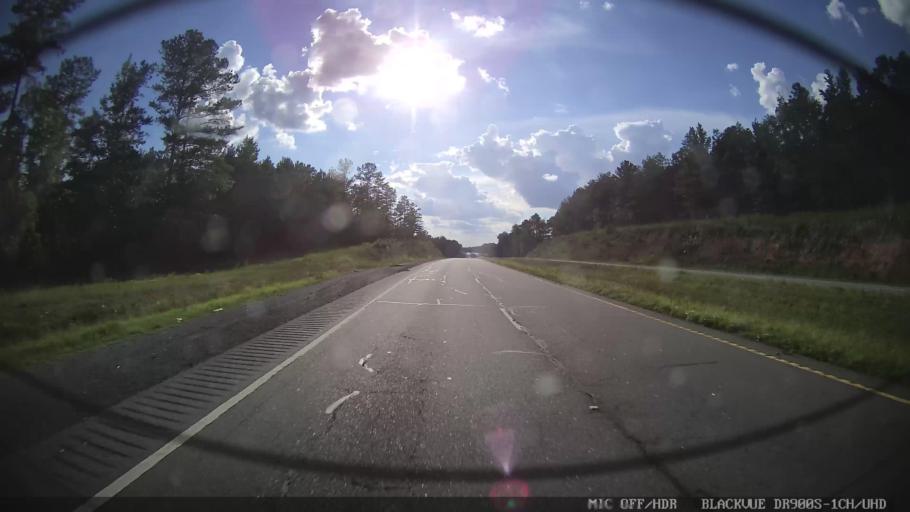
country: US
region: Georgia
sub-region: Bartow County
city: Euharlee
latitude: 34.2044
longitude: -85.0336
